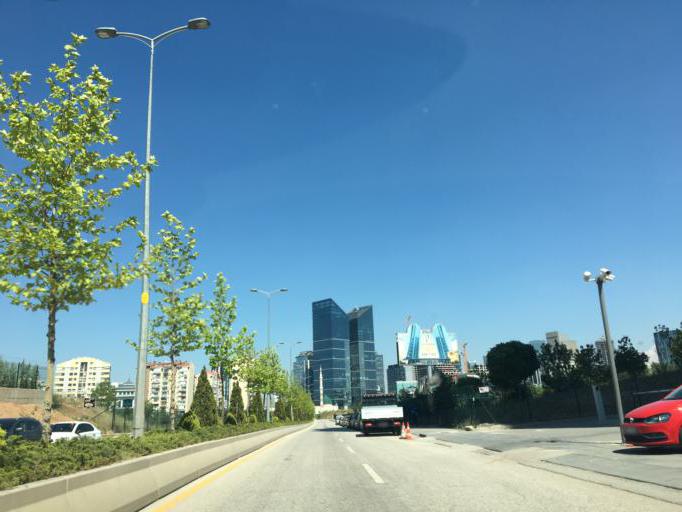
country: TR
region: Ankara
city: Ankara
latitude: 39.9126
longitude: 32.7964
